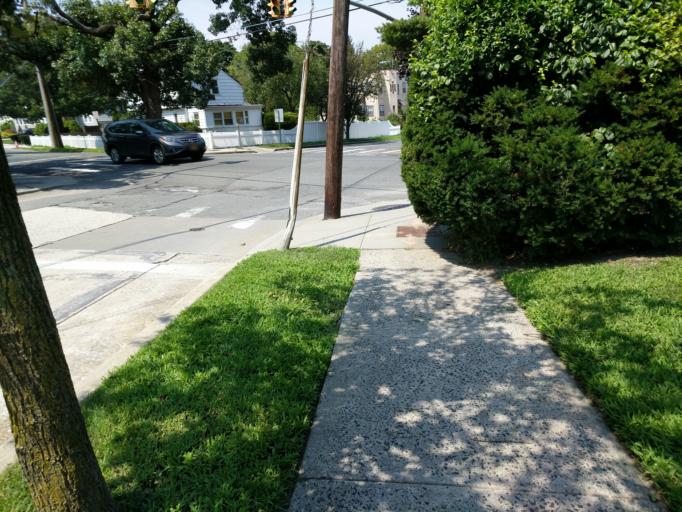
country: US
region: New York
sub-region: Nassau County
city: Cedarhurst
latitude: 40.6267
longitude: -73.7243
